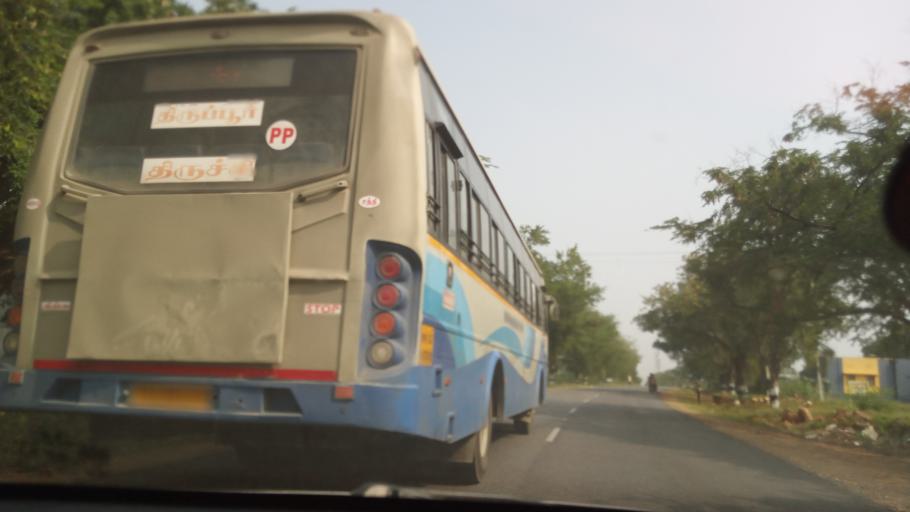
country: IN
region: Tamil Nadu
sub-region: Erode
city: Punjai Puliyampatti
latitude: 11.4158
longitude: 77.1938
